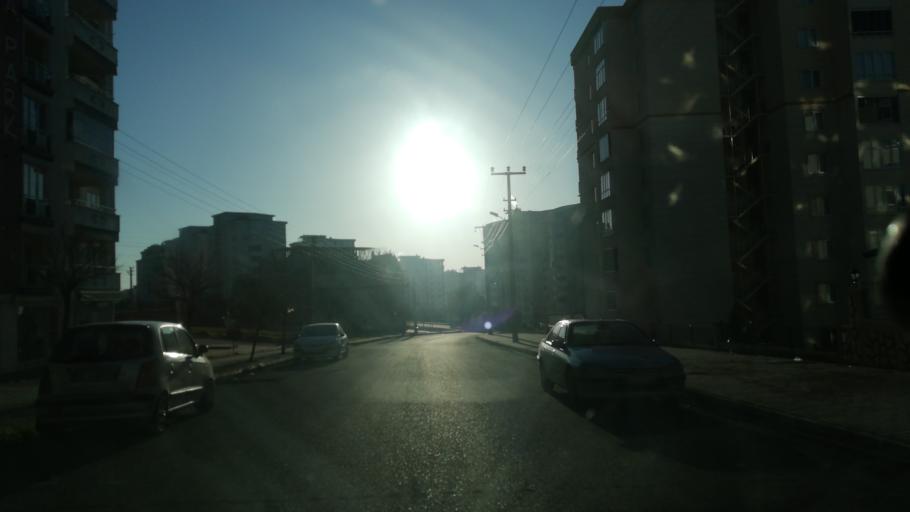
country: TR
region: Kahramanmaras
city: Kahramanmaras
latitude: 37.5983
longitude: 36.8871
